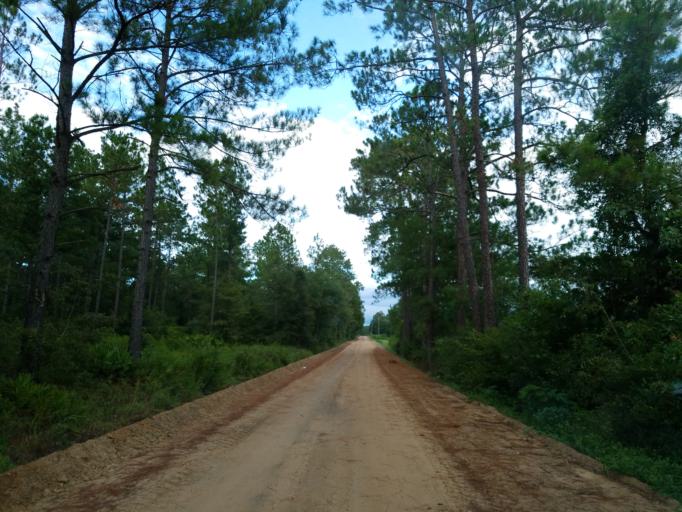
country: US
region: Georgia
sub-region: Cook County
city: Sparks
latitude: 31.2354
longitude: -83.4543
